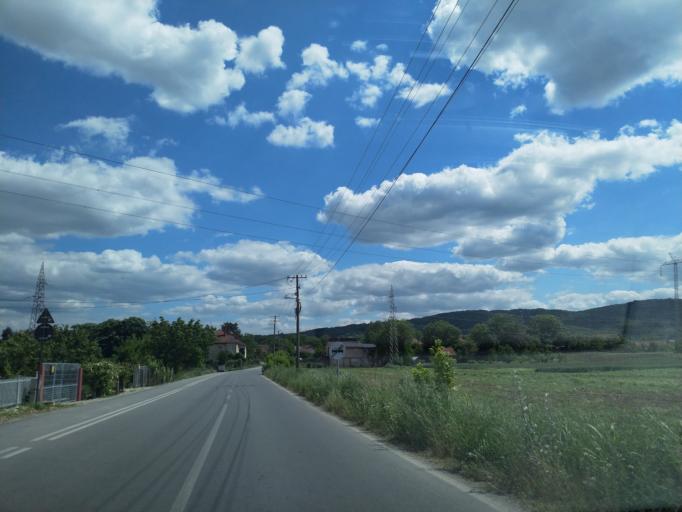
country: RS
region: Central Serbia
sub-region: Pomoravski Okrug
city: Jagodina
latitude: 43.9530
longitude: 21.2909
